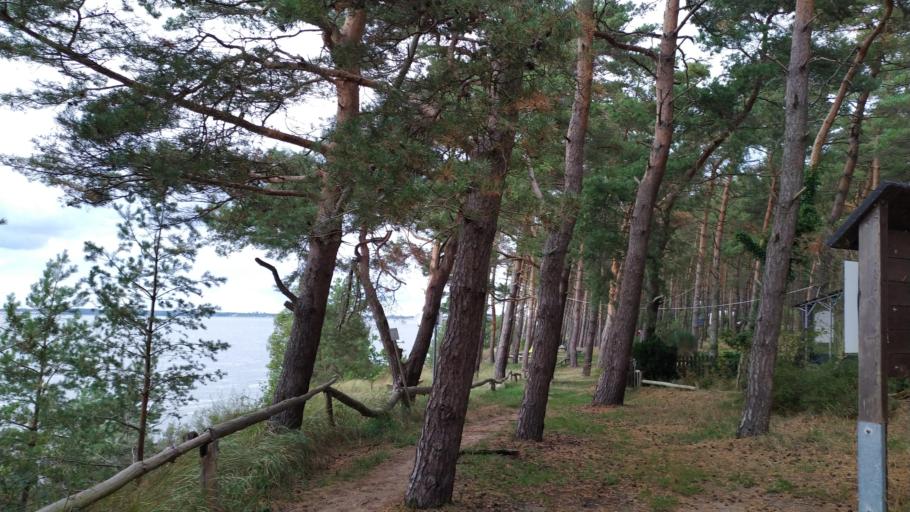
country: DE
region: Mecklenburg-Vorpommern
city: Lassan
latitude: 54.0073
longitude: 13.8532
